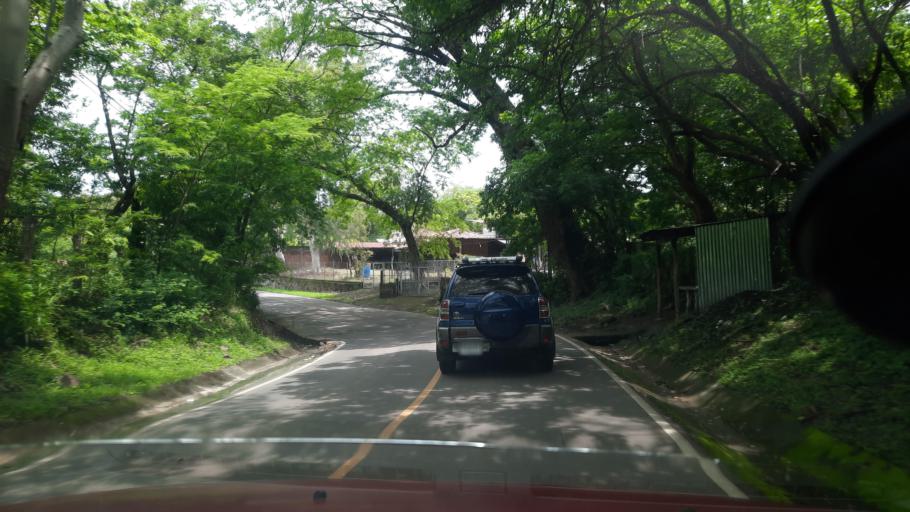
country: SV
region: La Union
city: Santa Rosa de Lima
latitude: 13.6478
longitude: -87.8512
